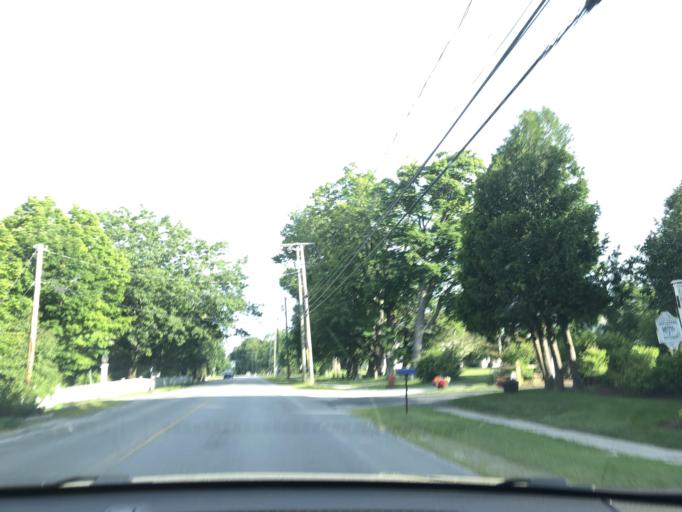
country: US
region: New Hampshire
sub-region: Merrimack County
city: New London
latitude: 43.4094
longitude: -71.9750
